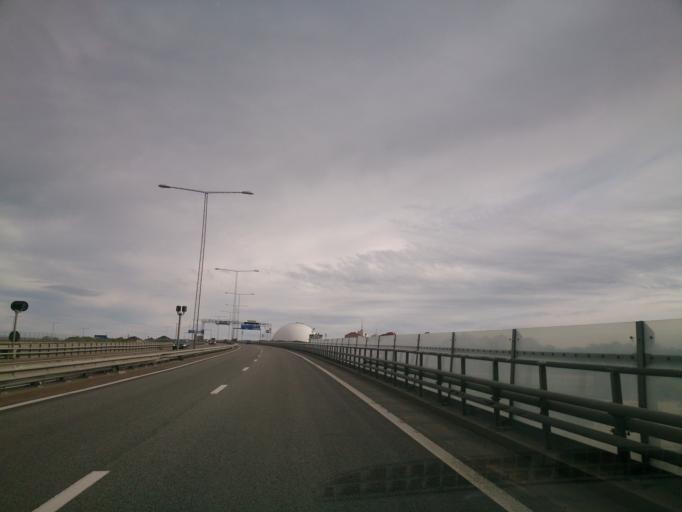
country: SE
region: Stockholm
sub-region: Stockholms Kommun
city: Arsta
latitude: 59.3054
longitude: 18.0756
